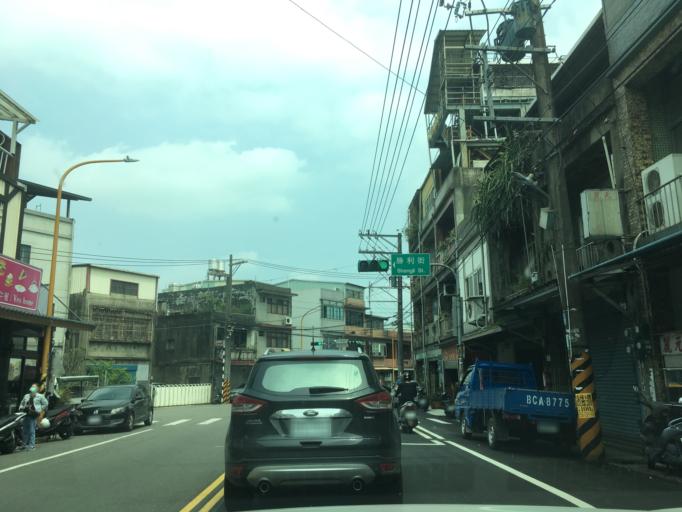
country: TW
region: Taiwan
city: Daxi
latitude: 24.8754
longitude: 121.2866
